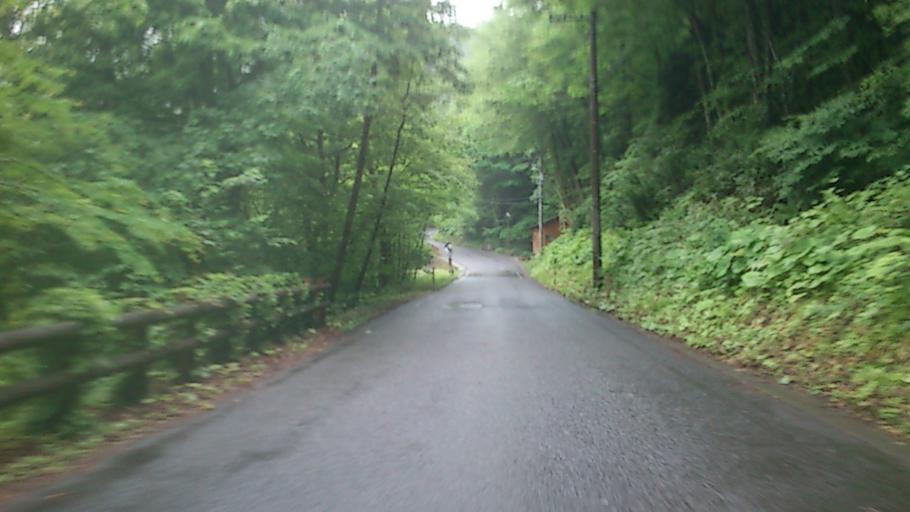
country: JP
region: Akita
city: Noshiromachi
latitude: 40.5658
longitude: 139.9781
